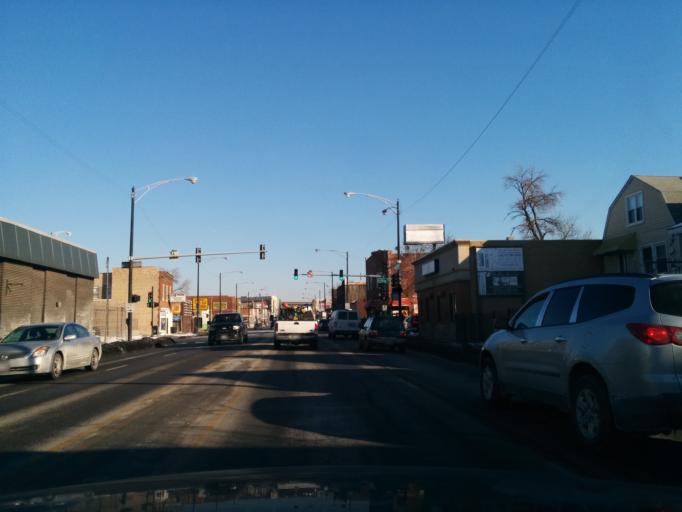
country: US
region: Illinois
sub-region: Cook County
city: Lincolnwood
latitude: 41.9492
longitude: -87.7472
